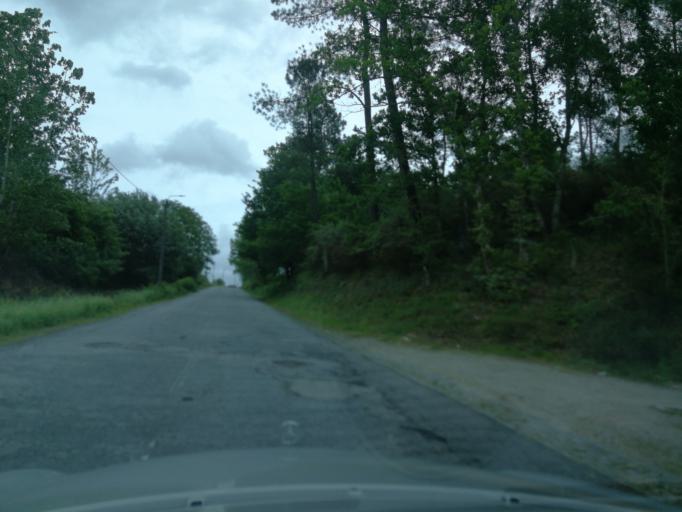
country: PT
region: Braga
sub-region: Braga
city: Adaufe
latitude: 41.6053
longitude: -8.3915
